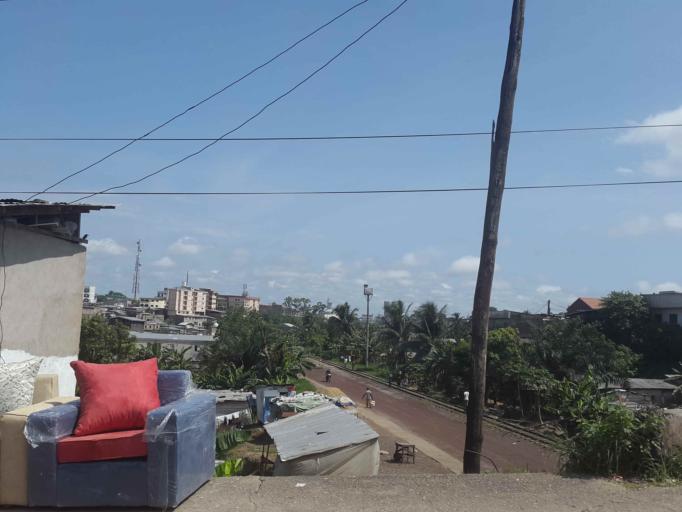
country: CM
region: Littoral
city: Douala
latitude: 4.0563
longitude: 9.7080
